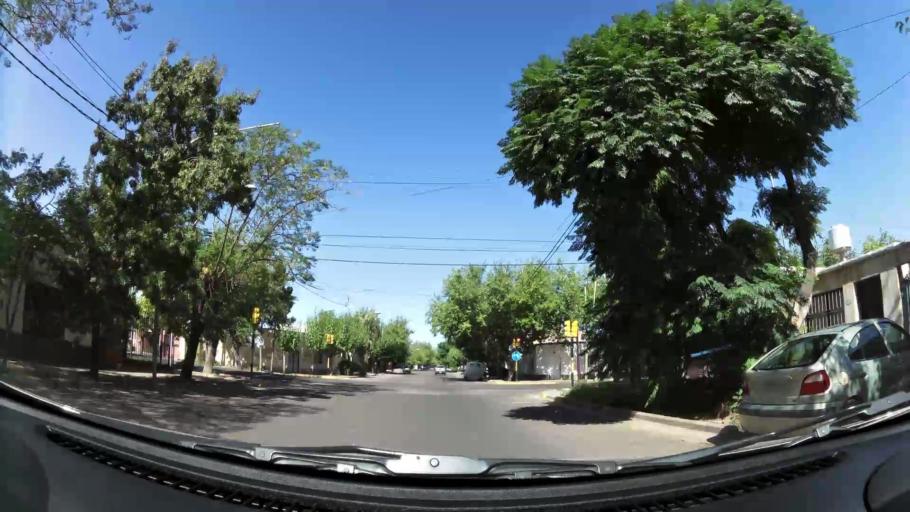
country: AR
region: Mendoza
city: Villa Nueva
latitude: -32.8996
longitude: -68.7842
